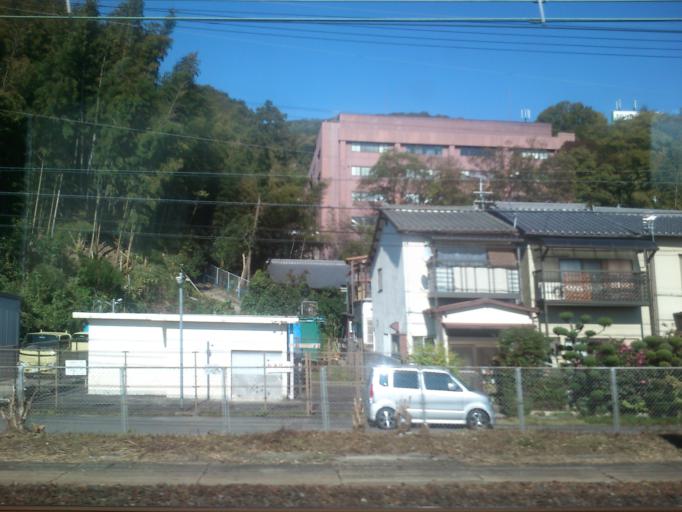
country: JP
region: Kyoto
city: Yawata
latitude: 34.8918
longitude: 135.6767
